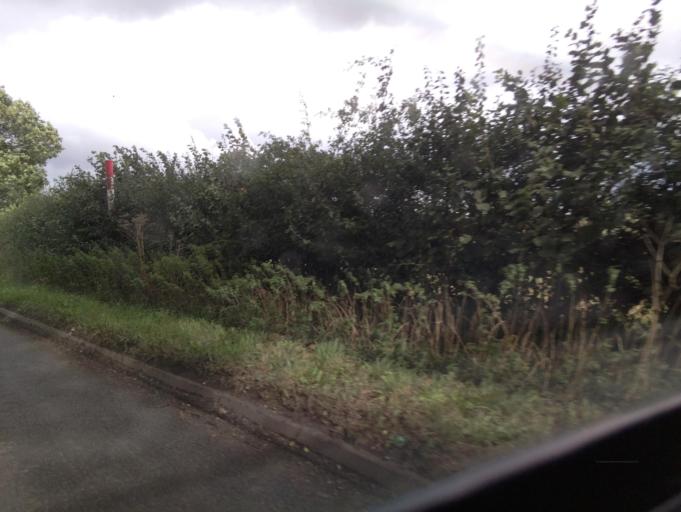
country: GB
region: England
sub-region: Staffordshire
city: Eccleshall
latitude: 52.8759
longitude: -2.2431
